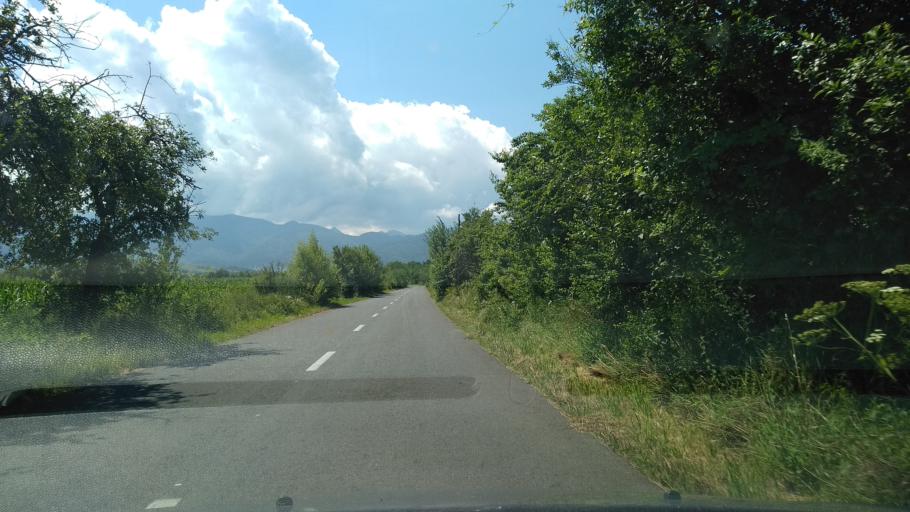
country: RO
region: Hunedoara
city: Salasu de Sus
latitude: 45.5185
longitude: 22.9599
